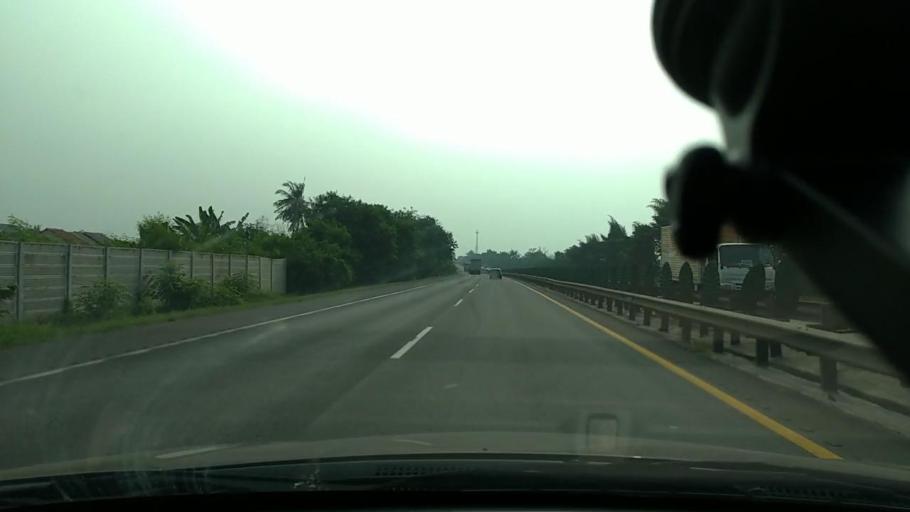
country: ID
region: Banten
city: Serang
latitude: -6.0949
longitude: 106.1633
